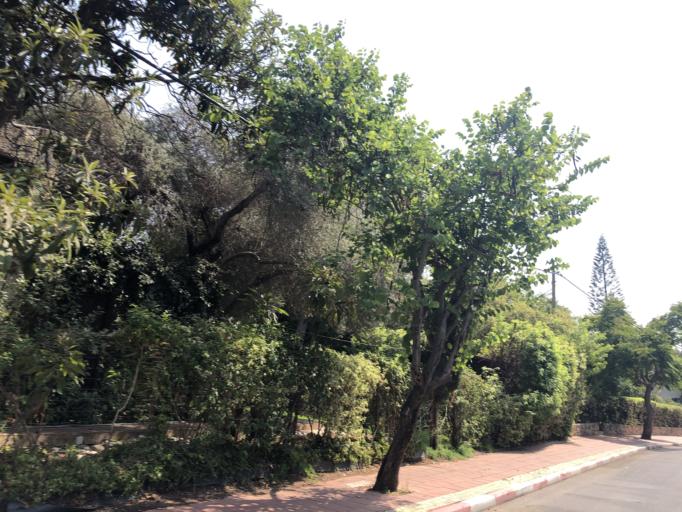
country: IL
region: Tel Aviv
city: Giv`atayim
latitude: 32.0528
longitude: 34.8311
